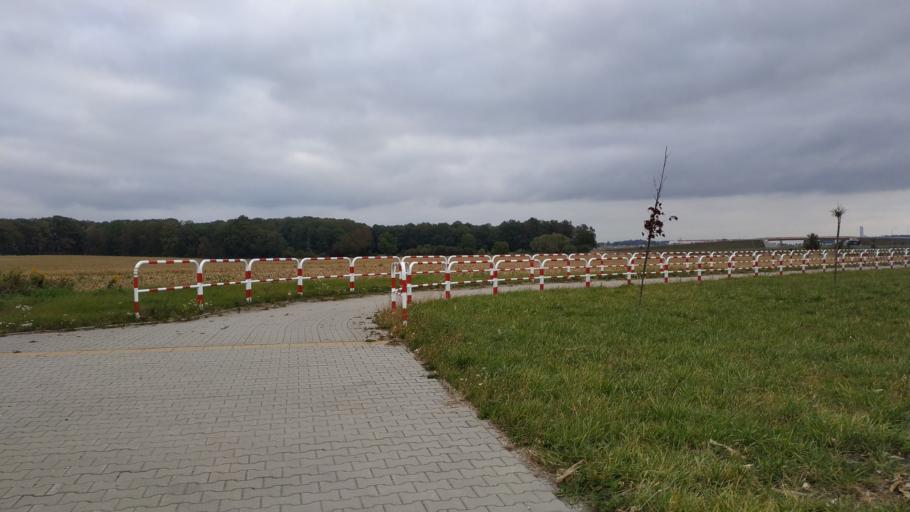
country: PL
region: Lower Silesian Voivodeship
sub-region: Powiat wroclawski
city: Tyniec Maly
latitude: 51.0241
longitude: 16.9046
